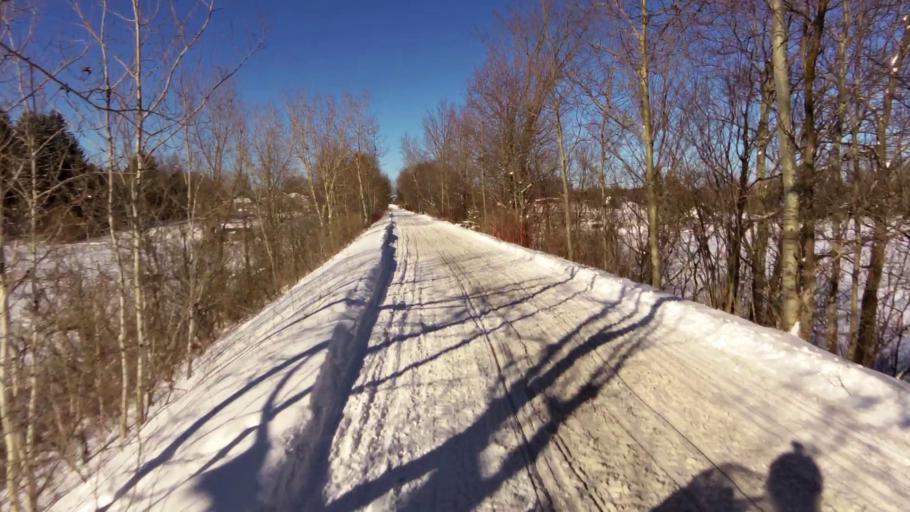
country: US
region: New York
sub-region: Chautauqua County
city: Mayville
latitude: 42.1605
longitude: -79.5857
